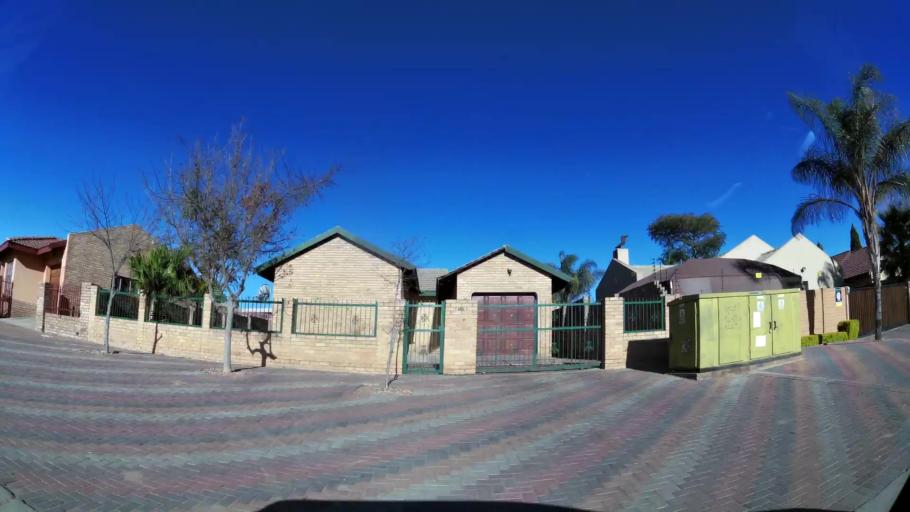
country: ZA
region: Limpopo
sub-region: Capricorn District Municipality
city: Polokwane
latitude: -23.8804
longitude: 29.4711
